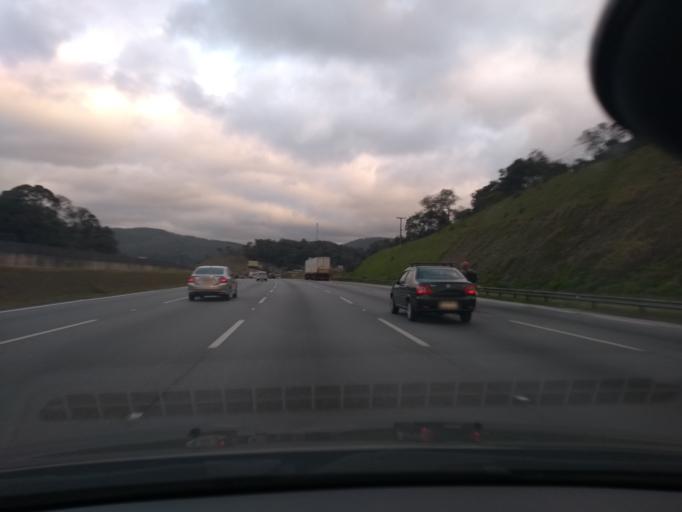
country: BR
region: Sao Paulo
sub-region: Cajamar
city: Cajamar
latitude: -23.3378
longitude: -46.8221
